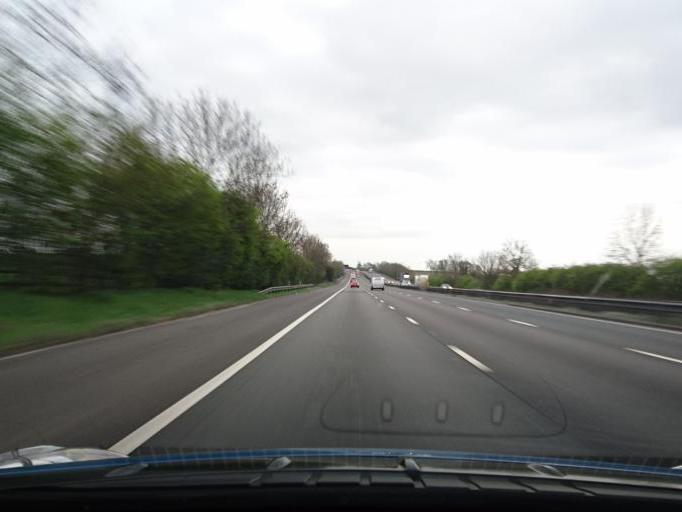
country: GB
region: England
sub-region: Staffordshire
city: Stone
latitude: 52.8515
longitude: -2.1601
